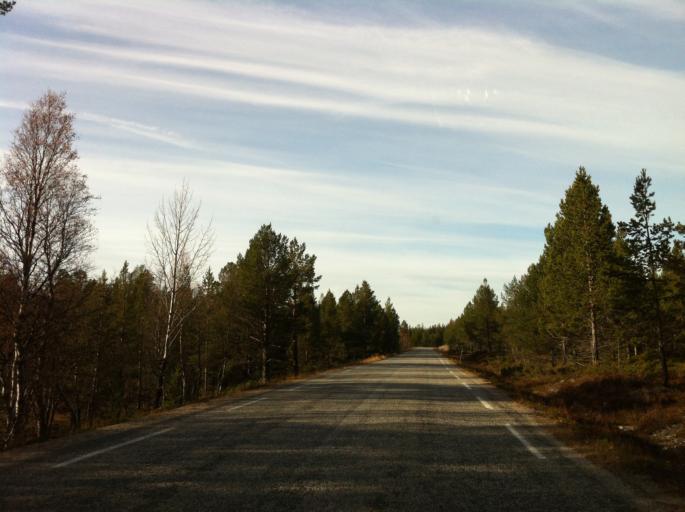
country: NO
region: Hedmark
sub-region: Engerdal
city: Engerdal
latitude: 62.1160
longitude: 12.0154
